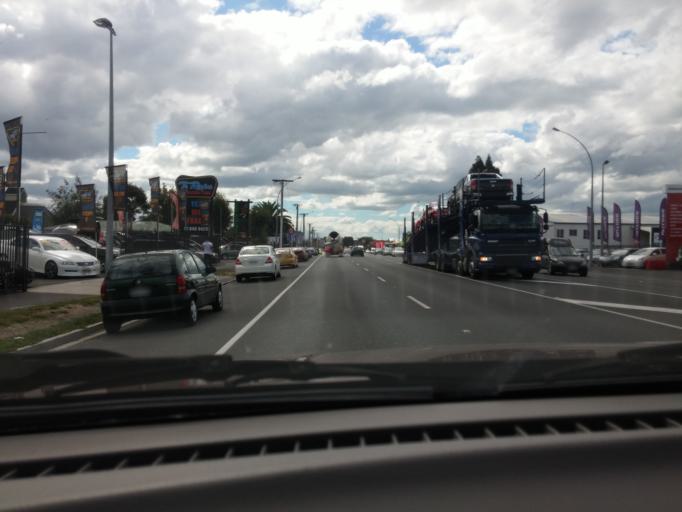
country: NZ
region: Waikato
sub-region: Hamilton City
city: Hamilton
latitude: -37.7937
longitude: 175.2604
